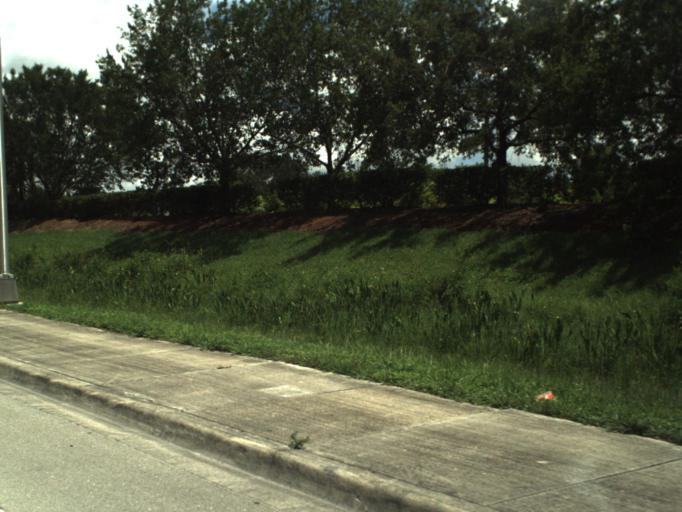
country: US
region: Florida
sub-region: Miami-Dade County
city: Country Club
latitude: 25.9789
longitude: -80.3258
